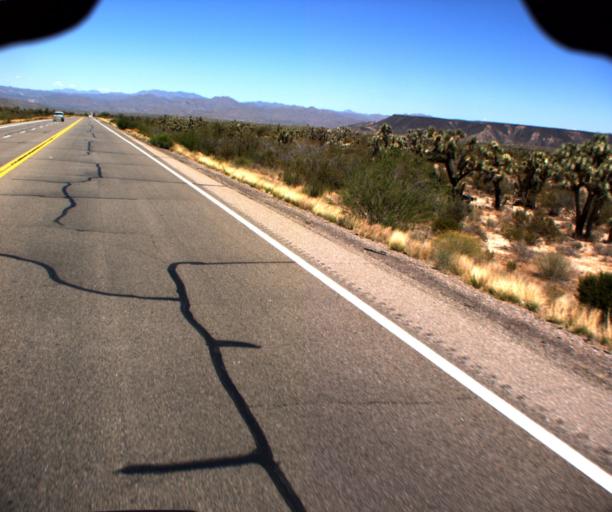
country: US
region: Arizona
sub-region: Yavapai County
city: Congress
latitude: 34.2883
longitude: -113.1086
